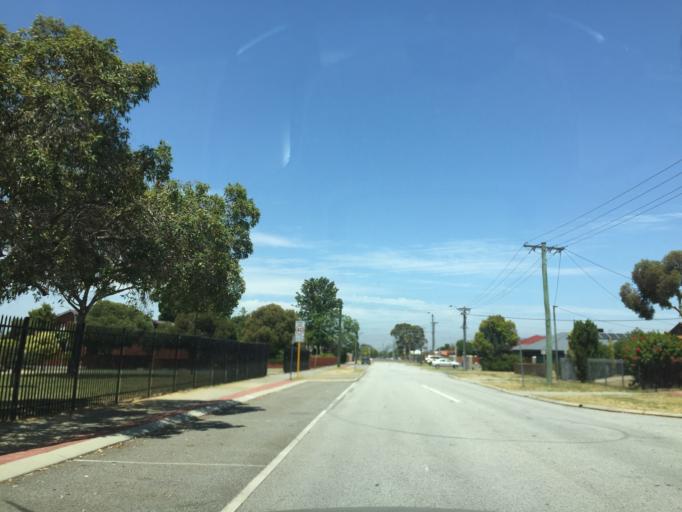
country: AU
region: Western Australia
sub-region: Canning
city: Queens Park
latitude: -32.0042
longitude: 115.9388
